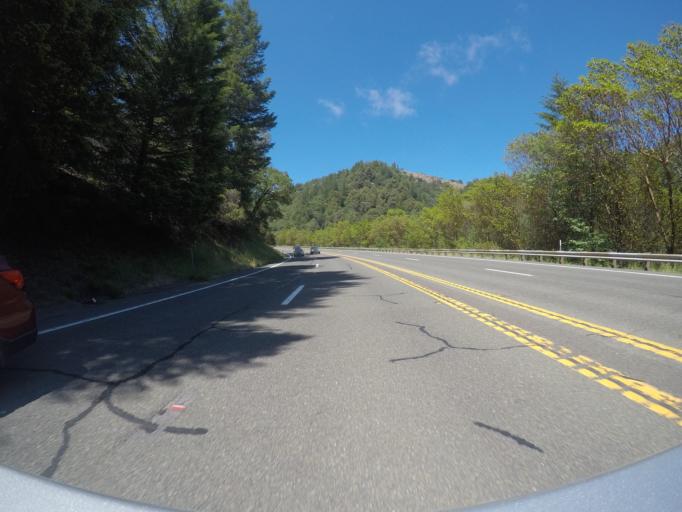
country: US
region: California
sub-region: Mendocino County
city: Laytonville
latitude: 39.6008
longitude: -123.4540
